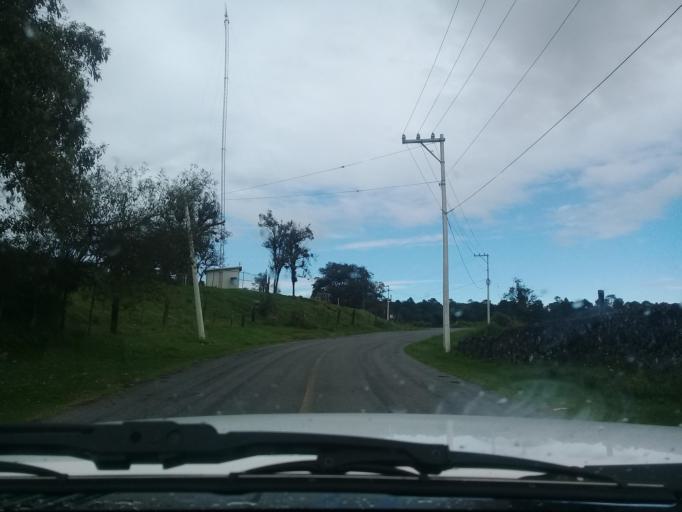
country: MX
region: Veracruz
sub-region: Acajete
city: La Joya
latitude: 19.6137
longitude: -97.0061
